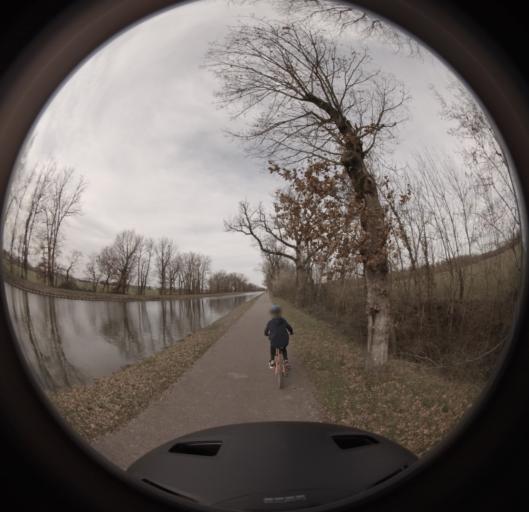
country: FR
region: Midi-Pyrenees
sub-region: Departement du Tarn-et-Garonne
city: Montech
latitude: 43.9741
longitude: 1.2484
